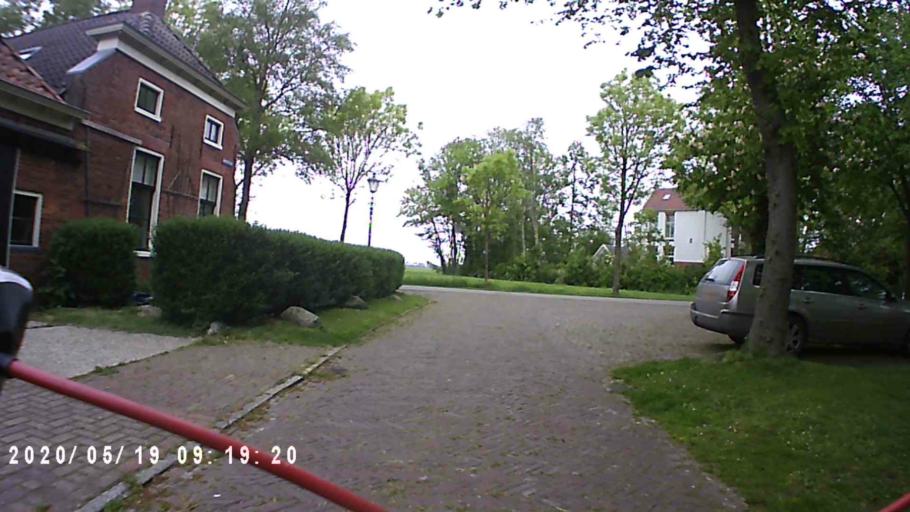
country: NL
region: Groningen
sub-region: Gemeente Zuidhorn
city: Oldehove
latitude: 53.2905
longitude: 6.3648
